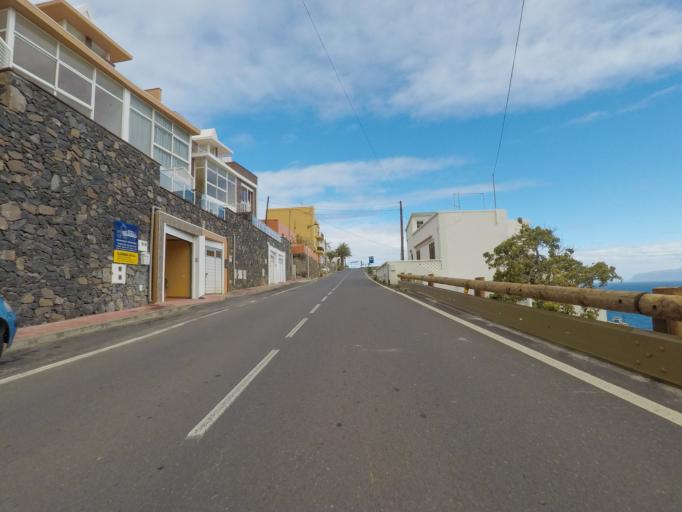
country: ES
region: Canary Islands
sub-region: Provincia de Santa Cruz de Tenerife
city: Hermigua
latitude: 28.1781
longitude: -17.1857
